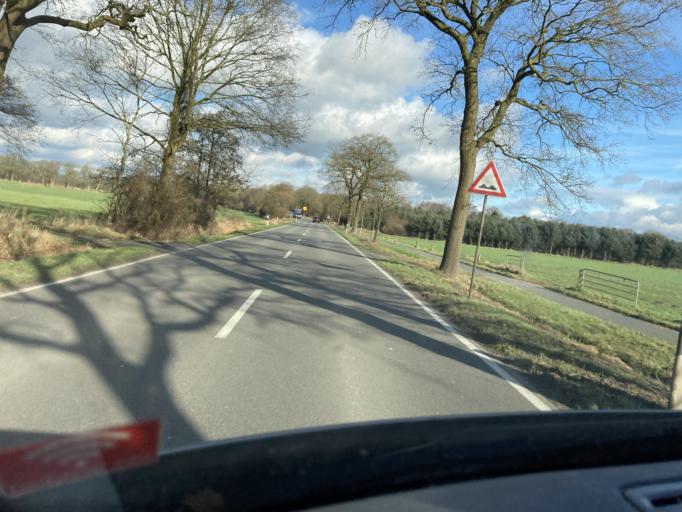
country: DE
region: Lower Saxony
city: Schwerinsdorf
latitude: 53.3178
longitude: 7.7627
